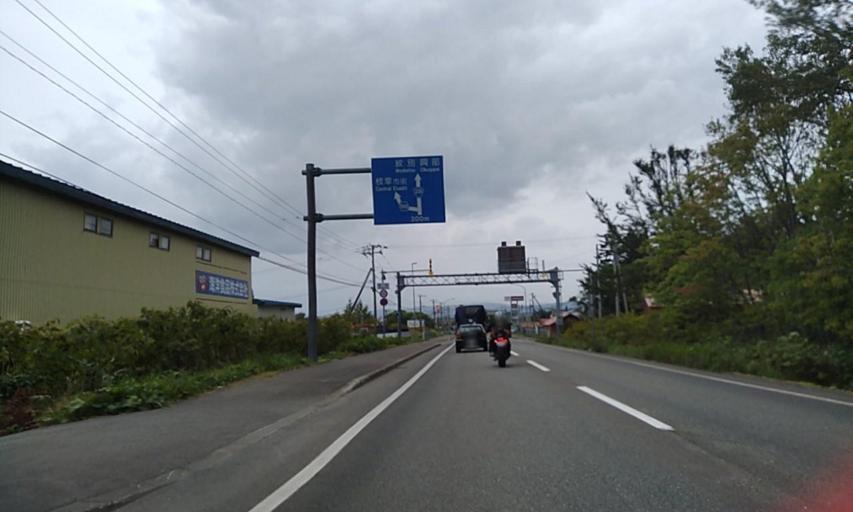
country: JP
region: Hokkaido
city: Nayoro
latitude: 44.9519
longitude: 142.5778
